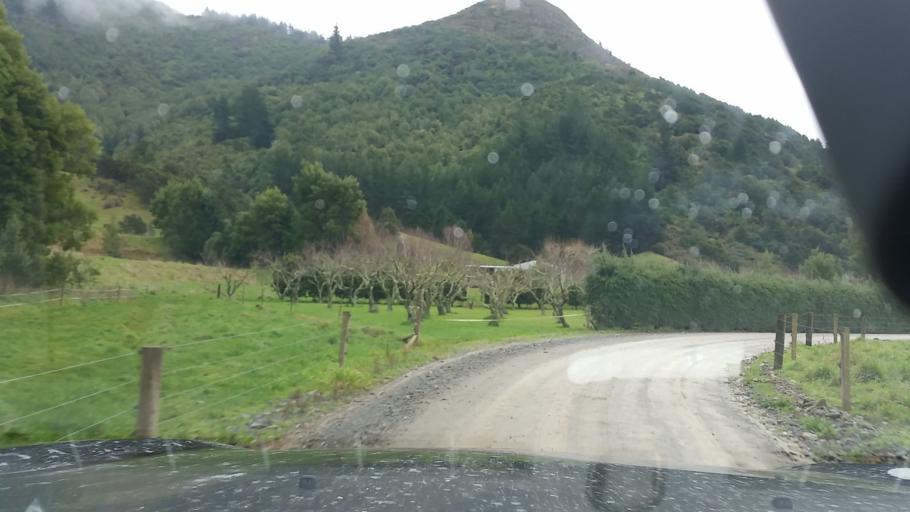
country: NZ
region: Marlborough
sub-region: Marlborough District
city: Picton
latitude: -41.3050
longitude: 173.6636
